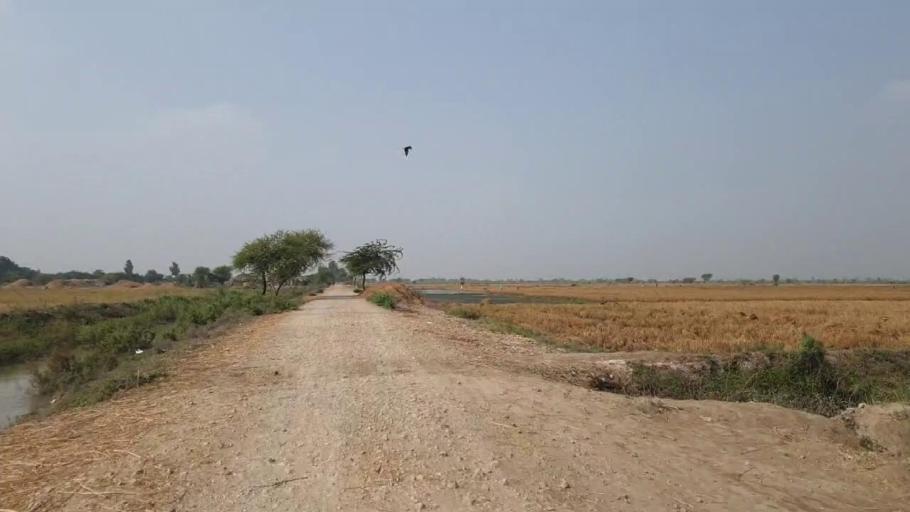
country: PK
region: Sindh
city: Kario
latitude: 24.7602
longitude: 68.5399
